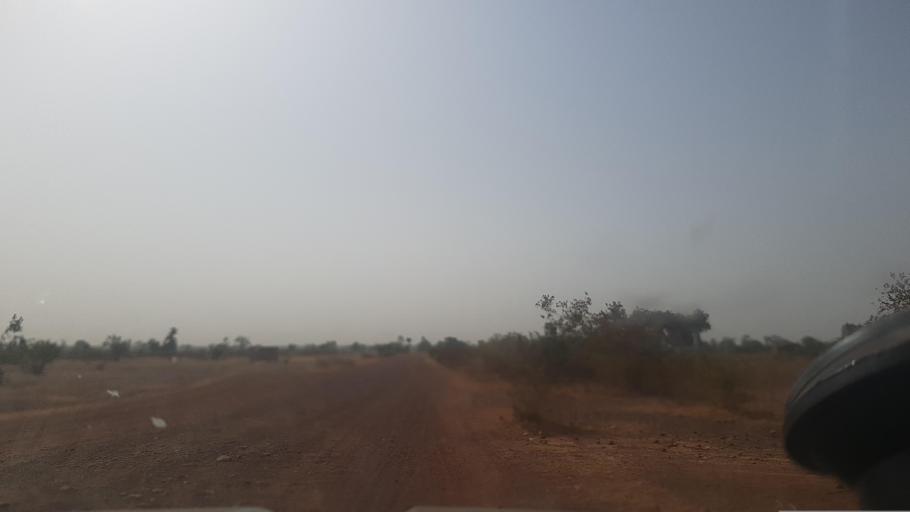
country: ML
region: Segou
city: Baroueli
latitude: 13.1560
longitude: -6.5169
